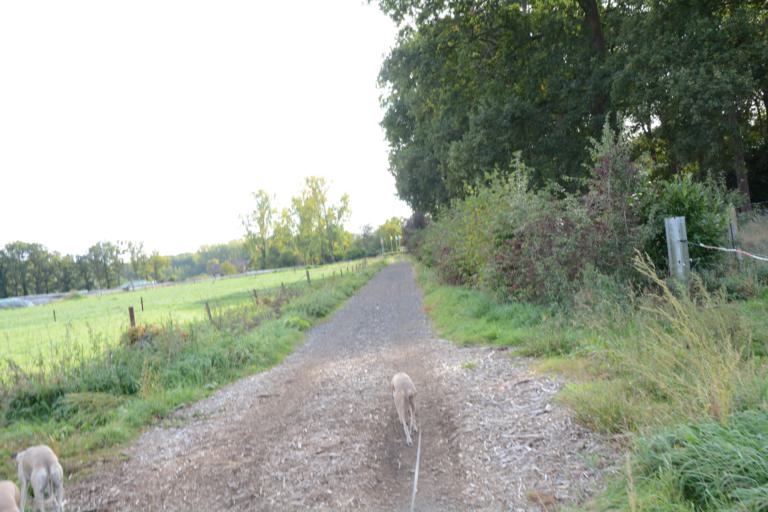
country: BE
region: Flanders
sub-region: Provincie Antwerpen
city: Sint-Amands
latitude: 51.0397
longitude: 4.2415
